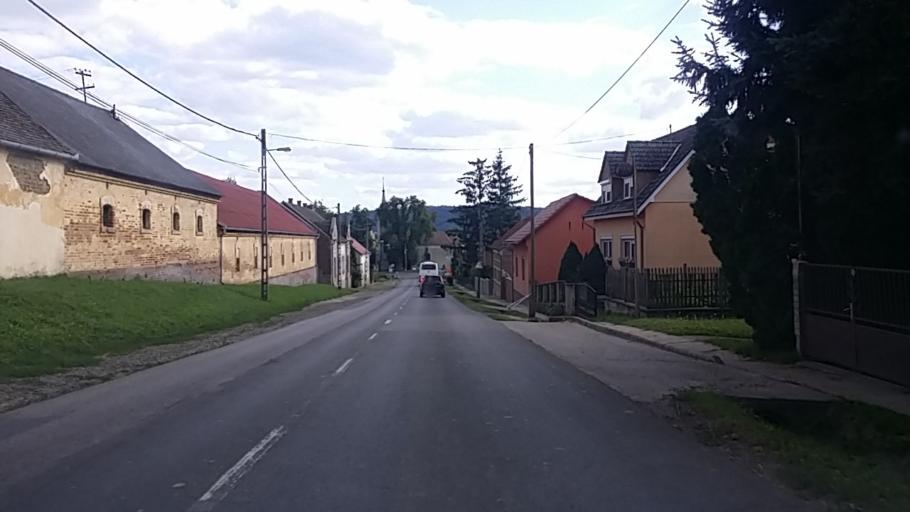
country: HU
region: Baranya
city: Sasd
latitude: 46.2238
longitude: 18.1215
